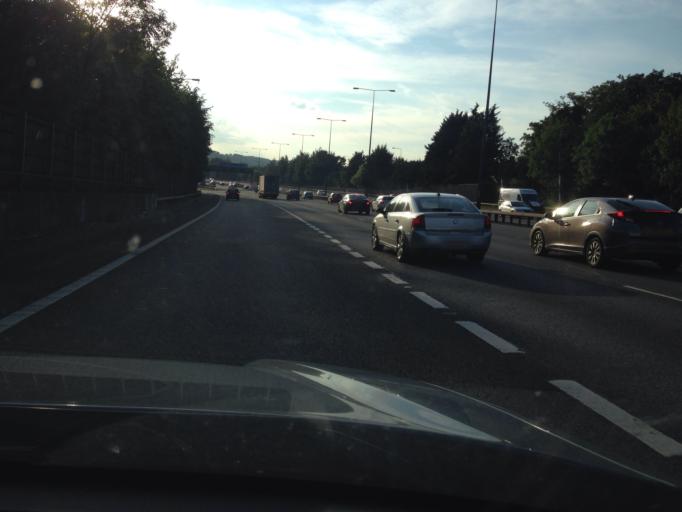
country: GB
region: England
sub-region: Buckinghamshire
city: Bourne End
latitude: 51.6019
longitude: -0.6868
